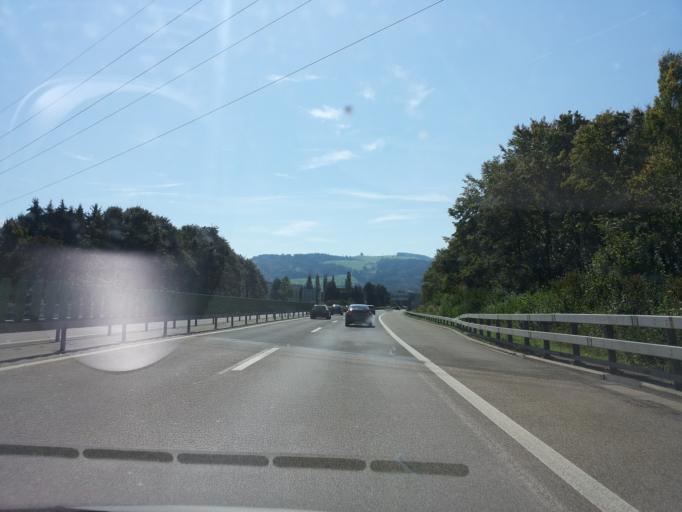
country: CH
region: Zug
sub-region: Zug
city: Hunenberg
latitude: 47.1554
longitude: 8.4326
